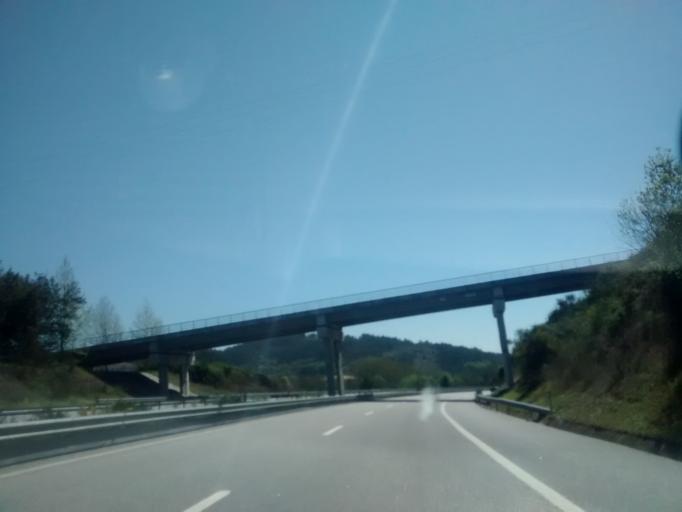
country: PT
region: Braga
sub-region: Guimaraes
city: Candoso
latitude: 41.4182
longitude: -8.3257
